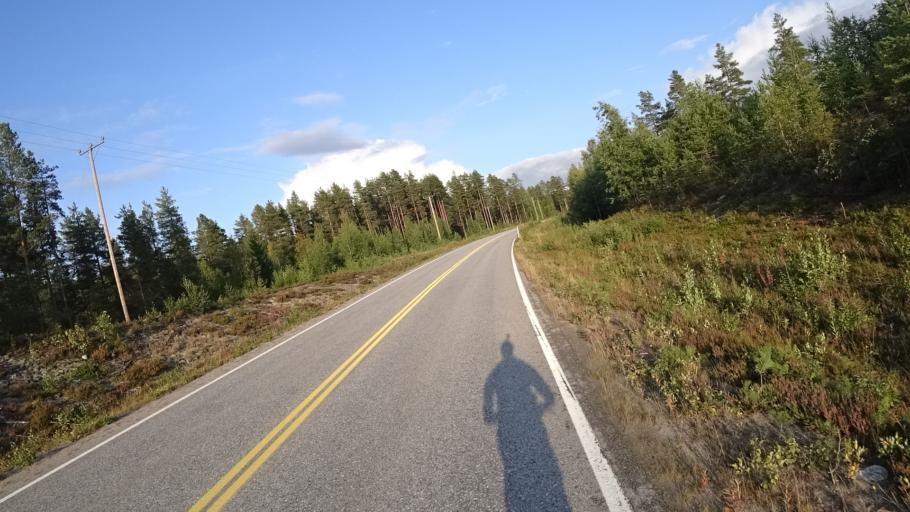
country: FI
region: North Karelia
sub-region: Joensuu
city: Ilomantsi
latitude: 62.6427
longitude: 31.0696
